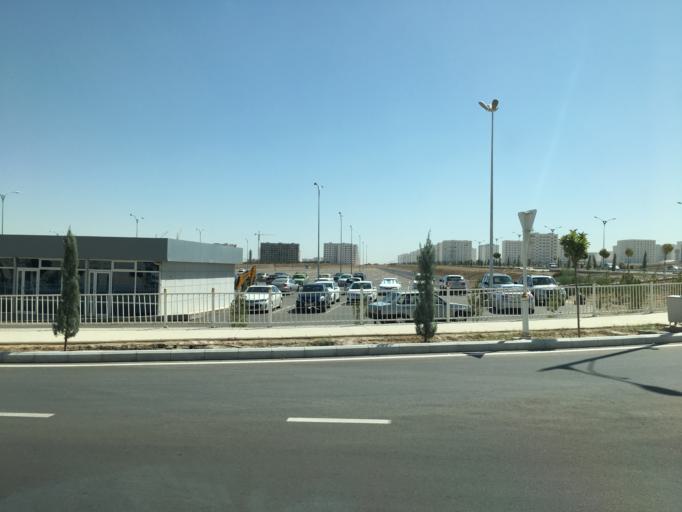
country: TM
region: Ahal
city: Ashgabat
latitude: 37.8959
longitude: 58.3969
